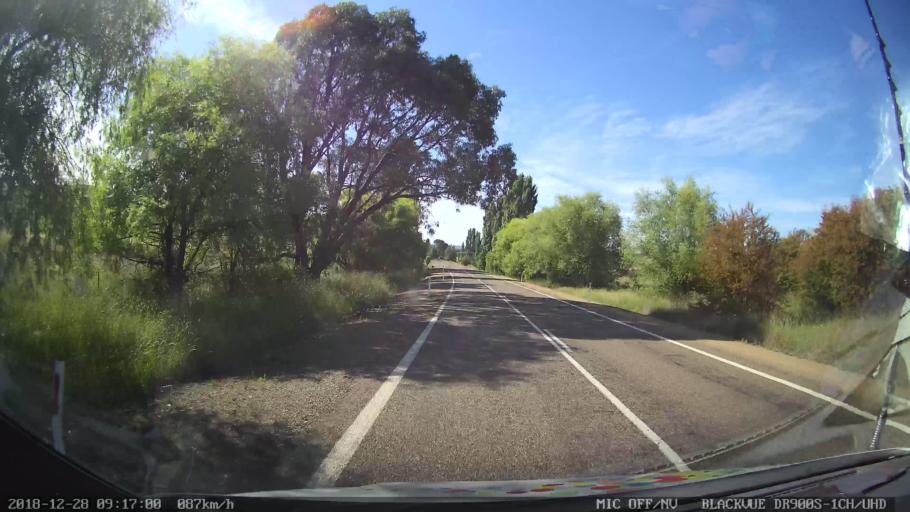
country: AU
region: New South Wales
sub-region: Upper Lachlan Shire
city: Crookwell
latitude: -34.3158
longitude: 149.3581
